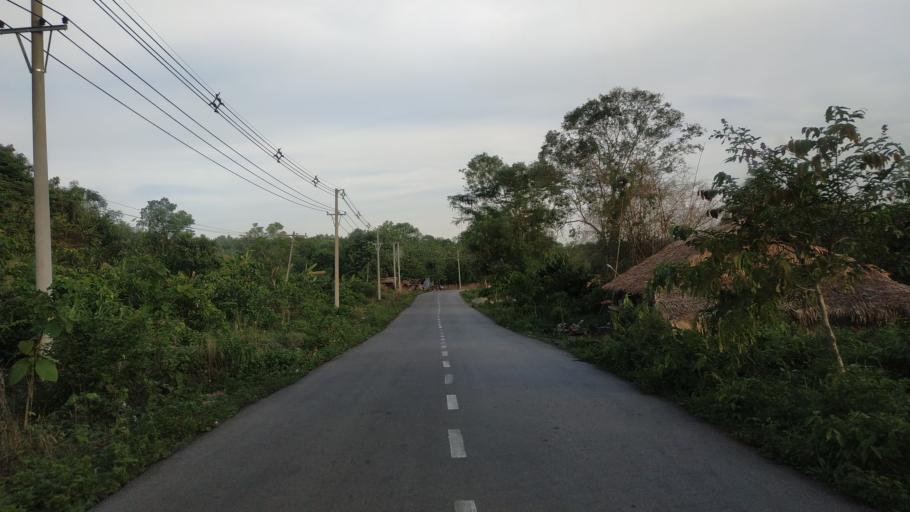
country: MM
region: Mon
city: Kyaikto
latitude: 17.4143
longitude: 97.0720
